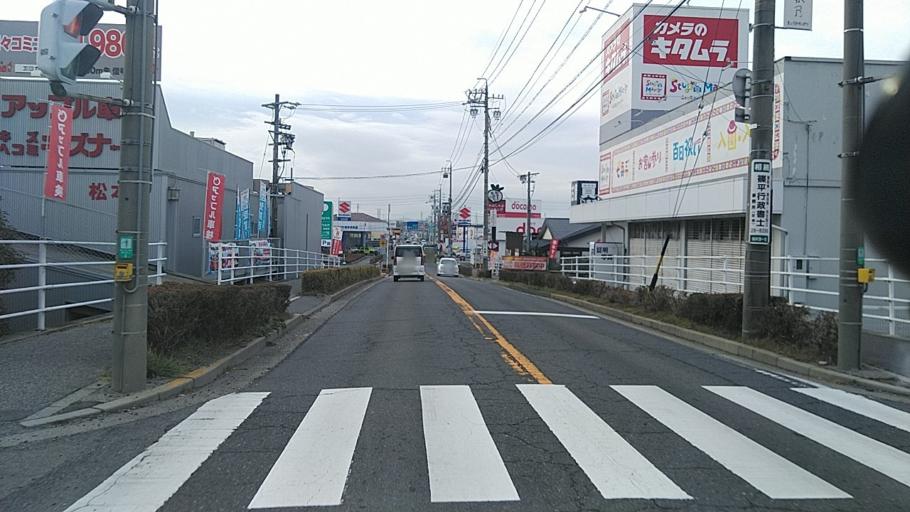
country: JP
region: Nagano
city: Matsumoto
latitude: 36.2166
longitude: 137.9797
